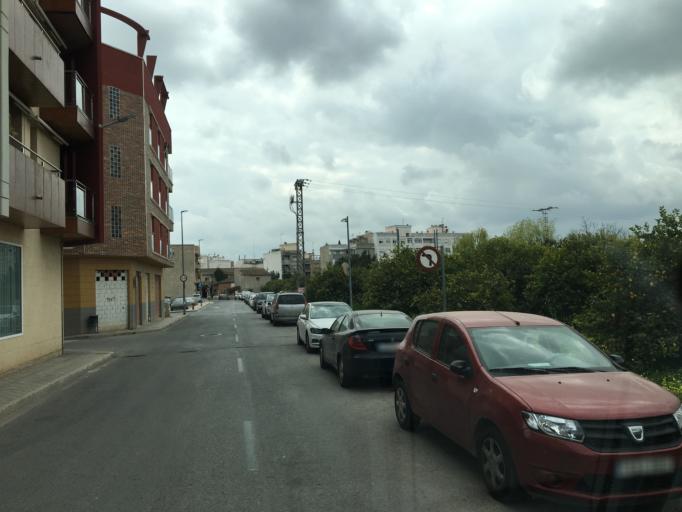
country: ES
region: Murcia
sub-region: Murcia
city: Beniel
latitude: 38.0457
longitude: -1.0046
